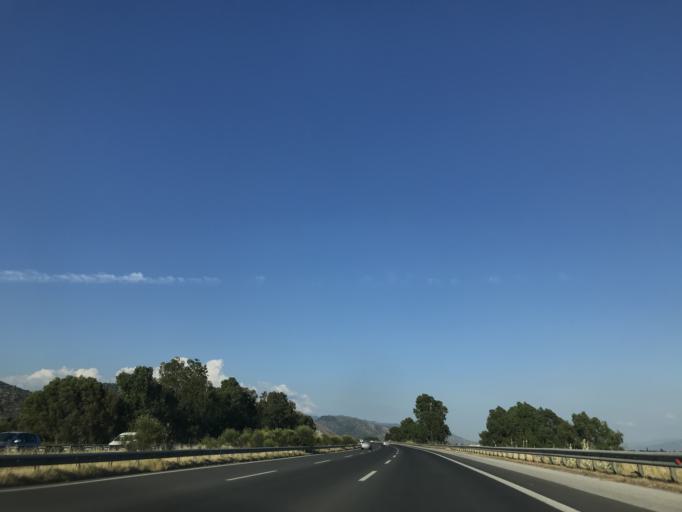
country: TR
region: Aydin
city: Germencik
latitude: 37.8692
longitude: 27.6560
